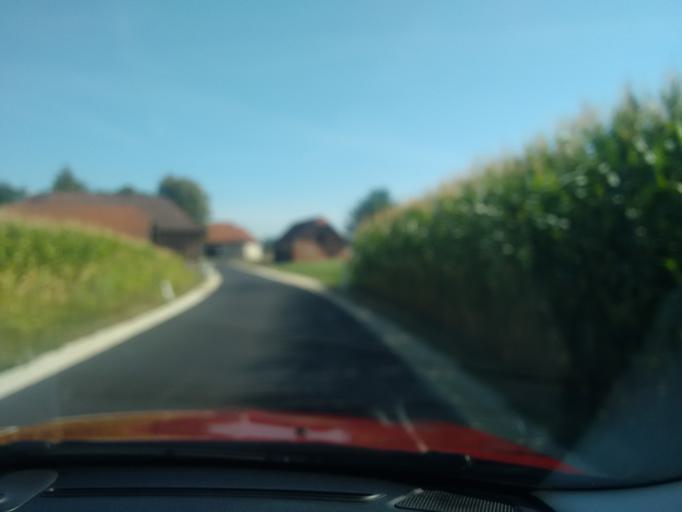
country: AT
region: Upper Austria
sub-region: Wels-Land
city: Sattledt
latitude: 48.0858
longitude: 14.0747
